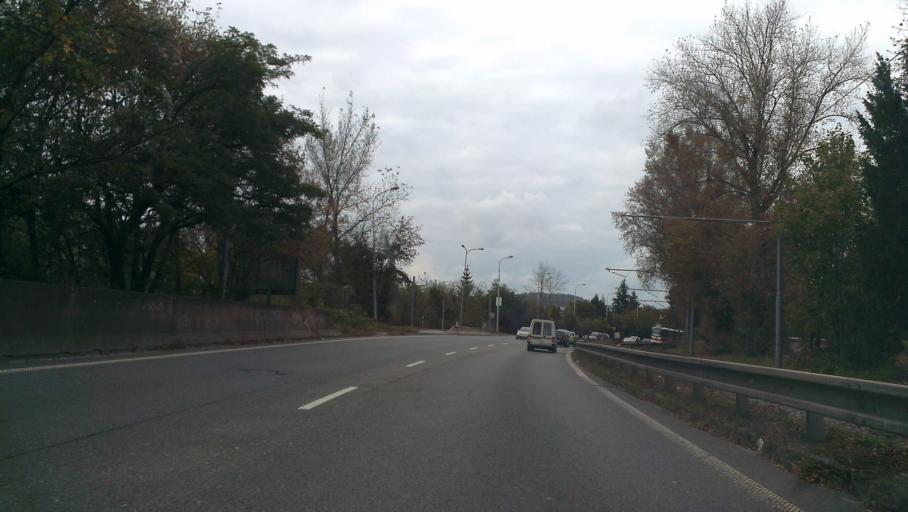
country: CZ
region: South Moravian
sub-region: Mesto Brno
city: Brno
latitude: 49.2021
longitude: 16.5678
